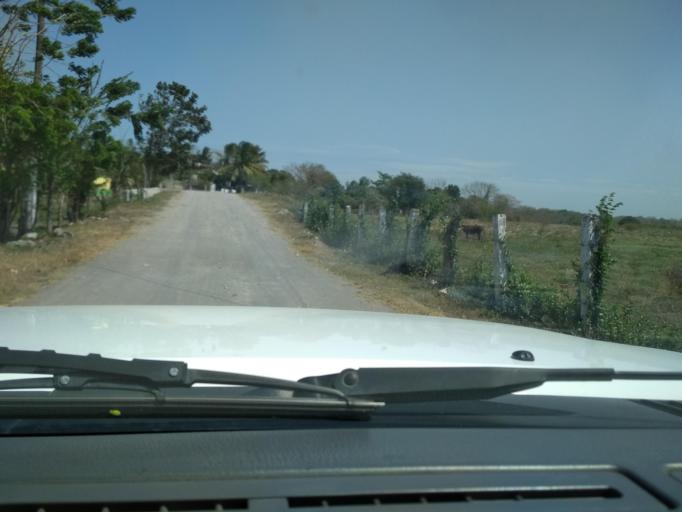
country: MX
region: Veracruz
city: Manlio Fabio Altamirano
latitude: 19.1551
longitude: -96.3300
